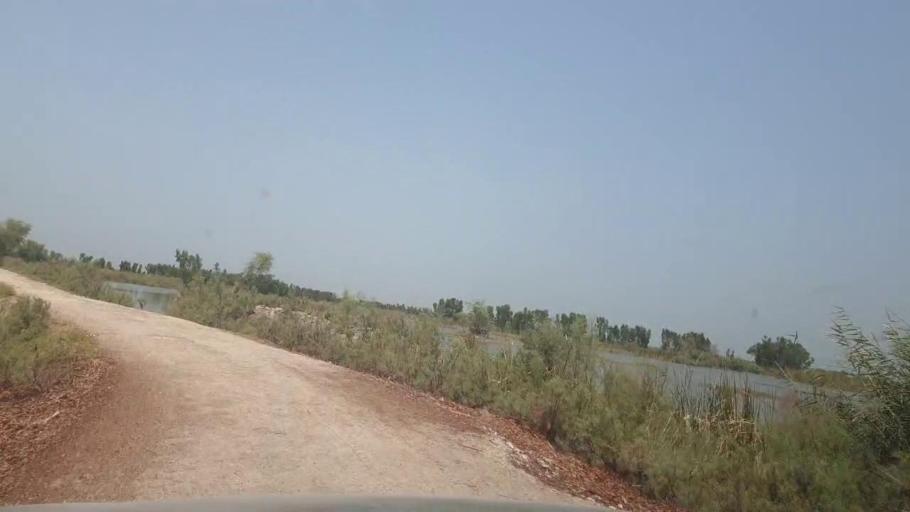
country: PK
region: Sindh
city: Lakhi
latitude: 27.8550
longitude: 68.6250
